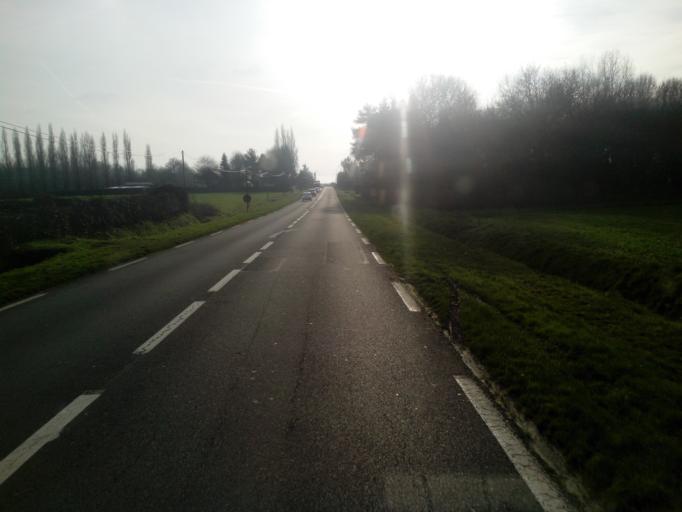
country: FR
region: Brittany
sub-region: Departement d'Ille-et-Vilaine
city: Saint-Meen-le-Grand
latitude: 48.1680
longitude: -2.2091
